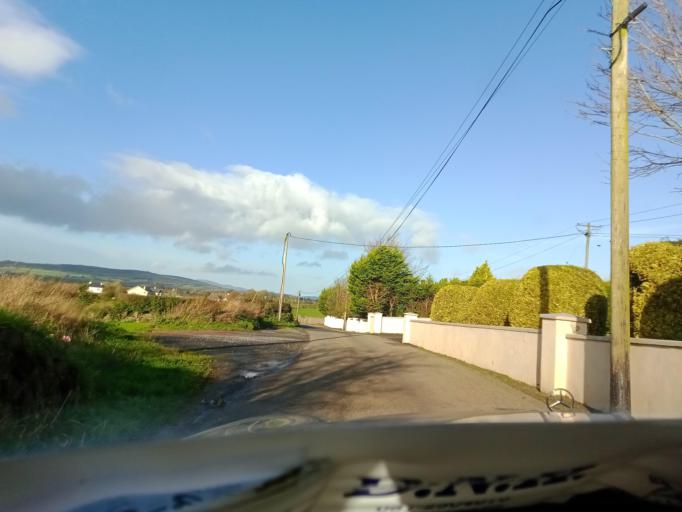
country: IE
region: Leinster
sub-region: Kilkenny
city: Mooncoin
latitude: 52.2780
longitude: -7.2488
